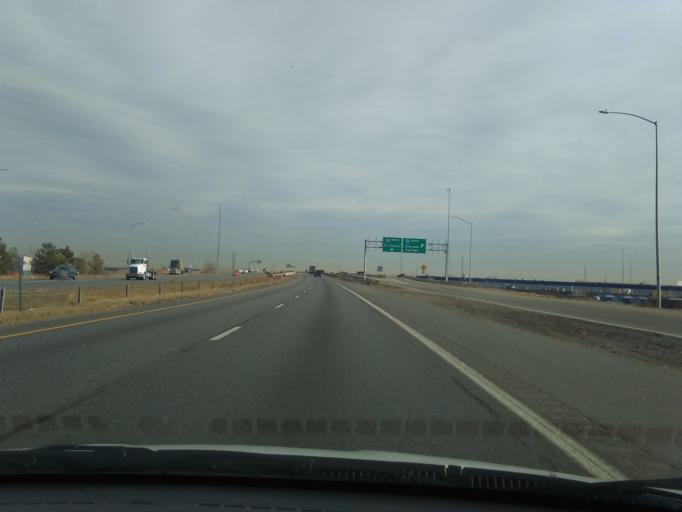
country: US
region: Colorado
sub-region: Adams County
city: Twin Lakes
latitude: 39.8132
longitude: -104.9906
